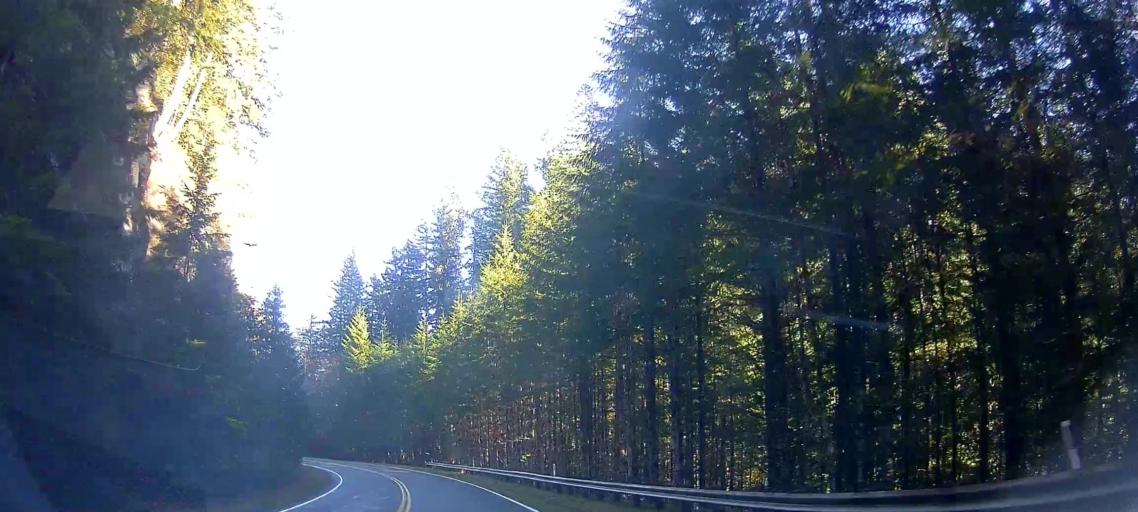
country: US
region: Washington
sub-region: Snohomish County
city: Darrington
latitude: 48.6484
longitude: -121.7137
